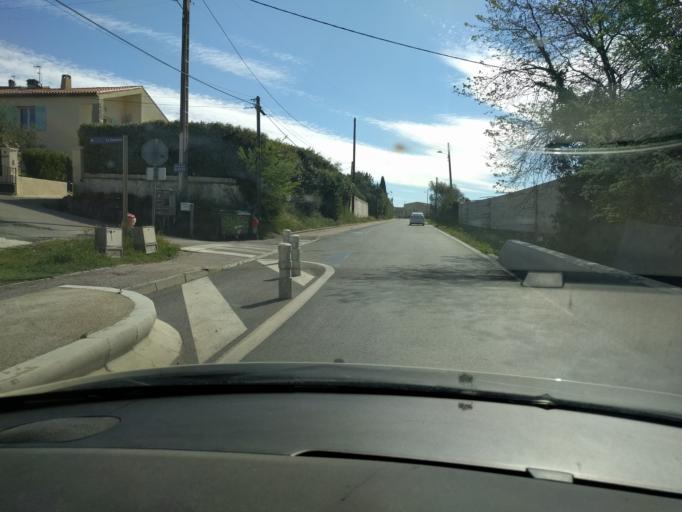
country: FR
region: Provence-Alpes-Cote d'Azur
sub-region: Departement du Var
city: Pierrefeu-du-Var
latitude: 43.2248
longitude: 6.1385
